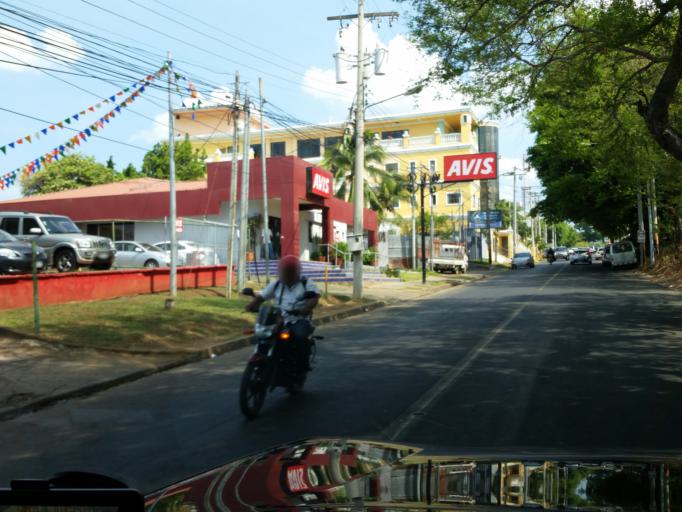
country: NI
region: Managua
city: Managua
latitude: 12.1157
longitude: -86.2654
